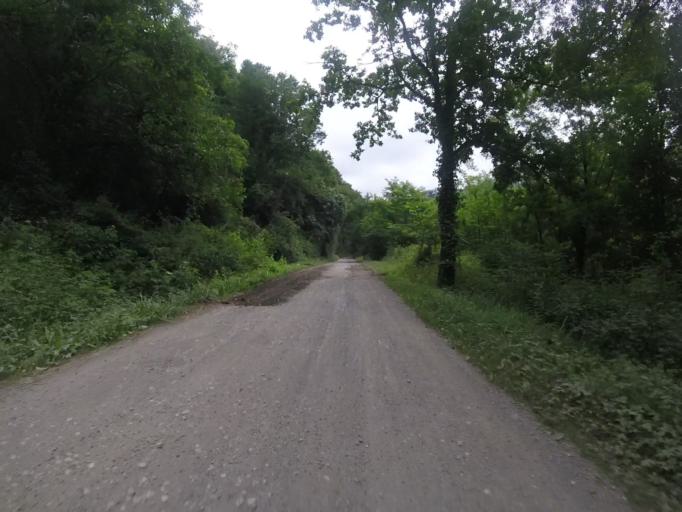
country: ES
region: Navarre
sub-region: Provincia de Navarra
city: Sunbilla
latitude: 43.1899
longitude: -1.6742
